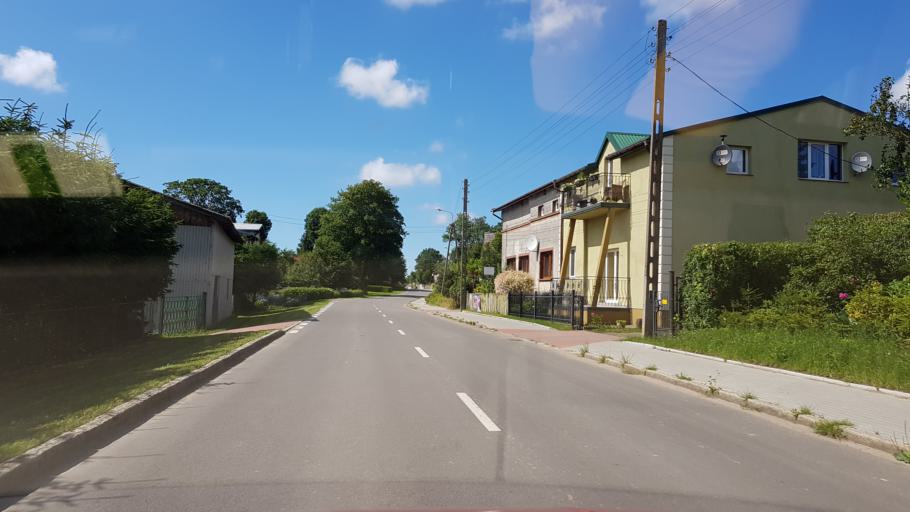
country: PL
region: West Pomeranian Voivodeship
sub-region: Powiat bialogardzki
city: Karlino
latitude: 54.1874
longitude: 15.9163
